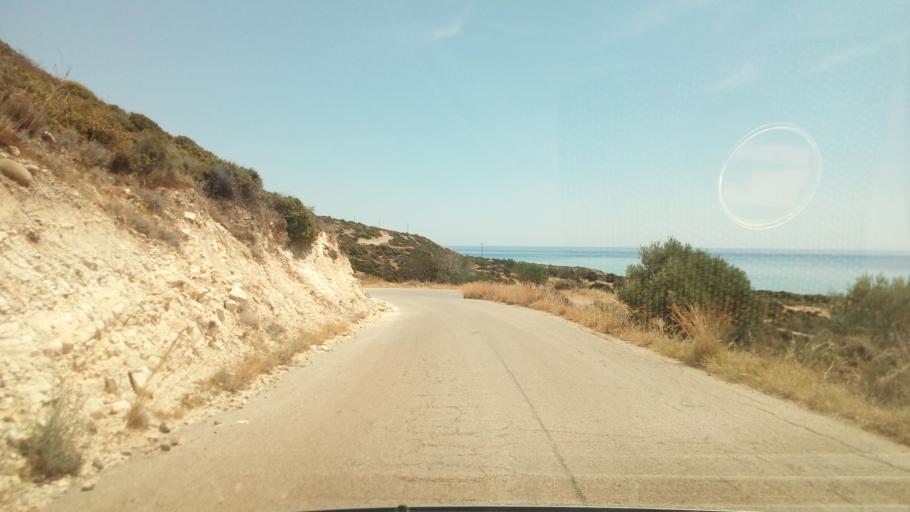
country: CY
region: Limassol
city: Pissouri
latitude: 34.6847
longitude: 32.5959
